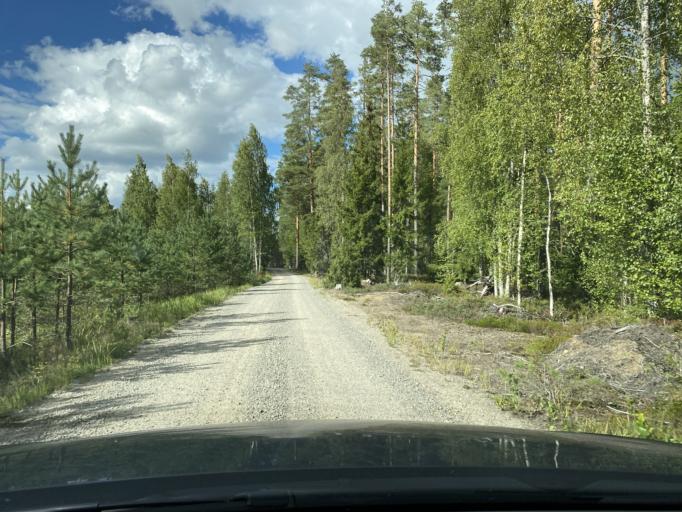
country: FI
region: Pirkanmaa
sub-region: Lounais-Pirkanmaa
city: Punkalaidun
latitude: 61.0864
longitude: 23.2572
